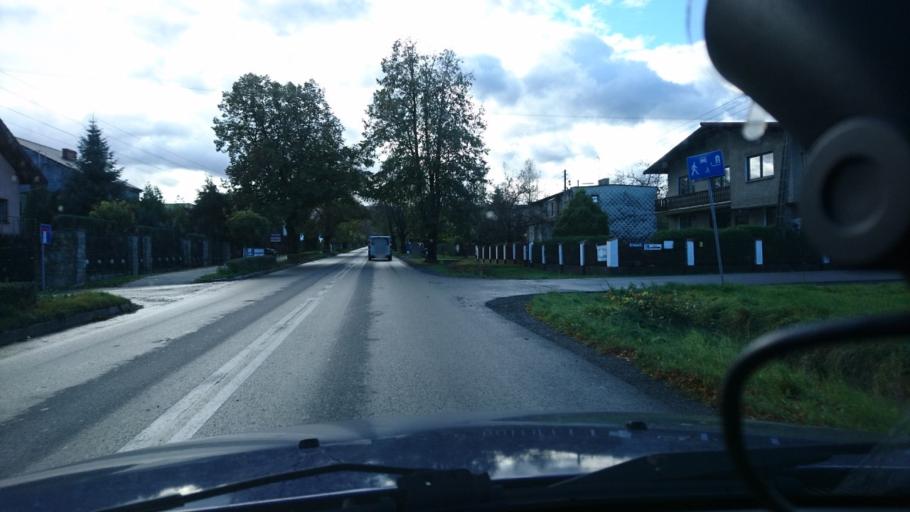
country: PL
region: Silesian Voivodeship
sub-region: Powiat bielski
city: Jasienica
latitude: 49.8100
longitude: 18.9205
